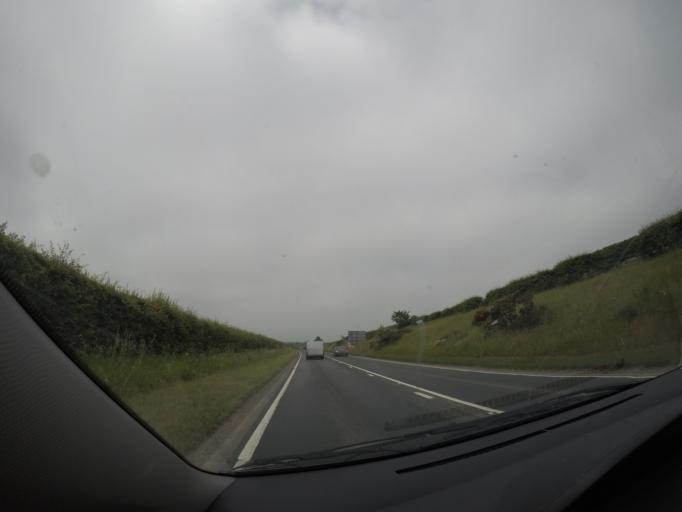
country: GB
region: England
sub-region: City and Borough of Leeds
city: Wetherby
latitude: 54.0096
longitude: -1.3627
